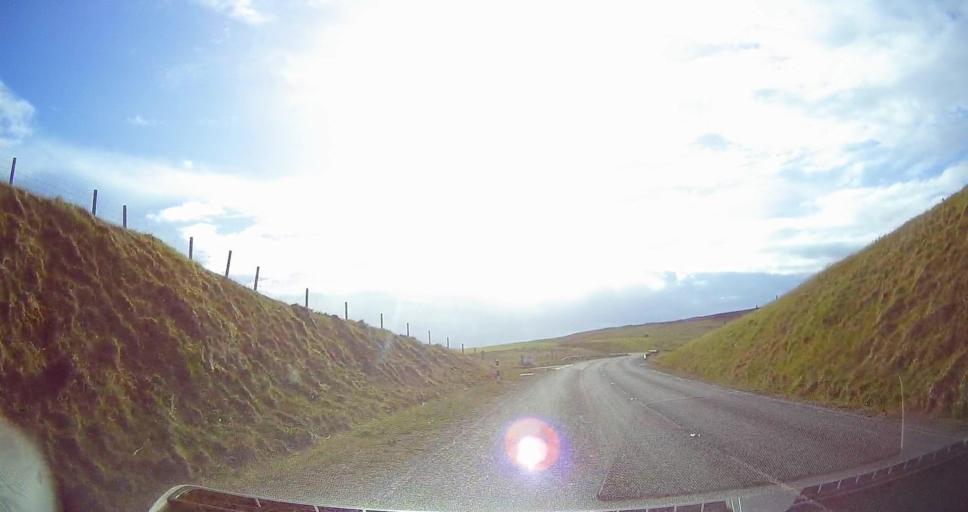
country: GB
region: Scotland
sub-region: Shetland Islands
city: Lerwick
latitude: 60.3704
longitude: -1.3110
